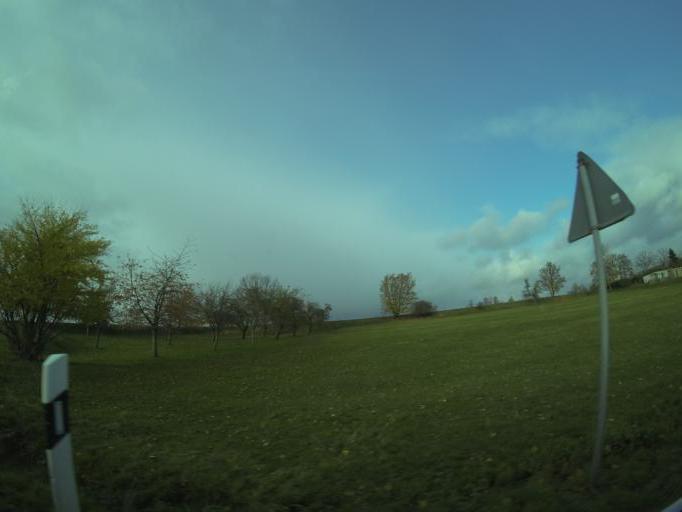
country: DE
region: Thuringia
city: Gossnitz
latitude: 50.8913
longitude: 12.3947
